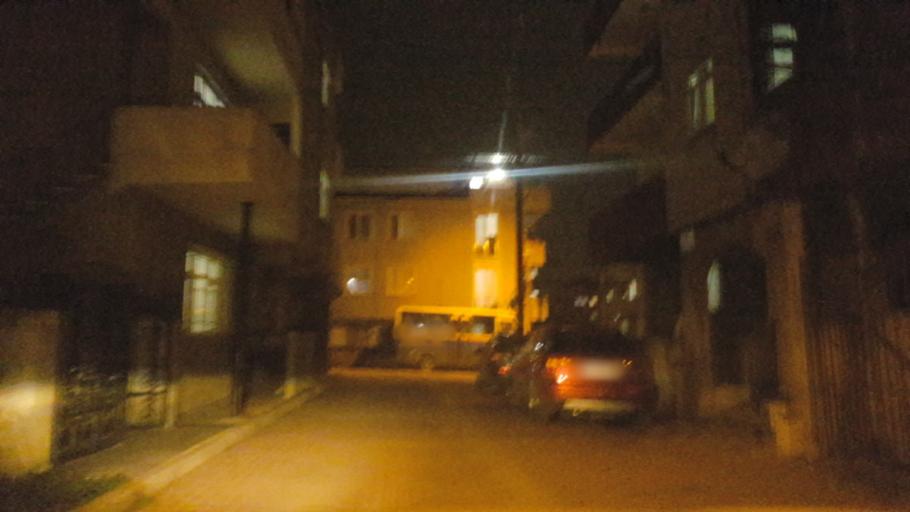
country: TR
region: Kocaeli
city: Darica
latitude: 40.7738
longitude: 29.3866
